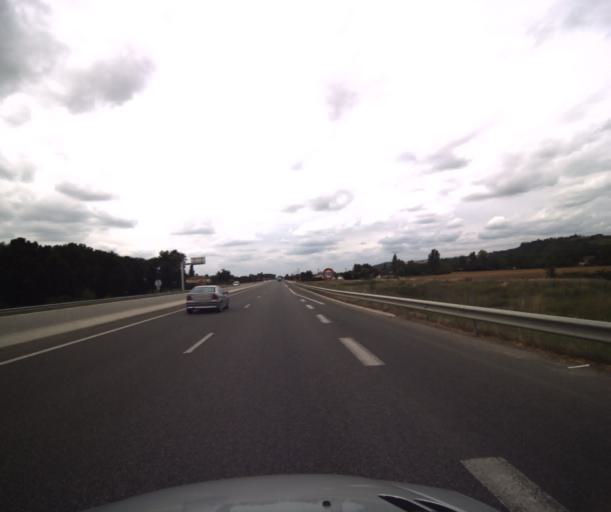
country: FR
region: Midi-Pyrenees
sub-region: Departement de la Haute-Garonne
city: Vernet
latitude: 43.4497
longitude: 1.4194
